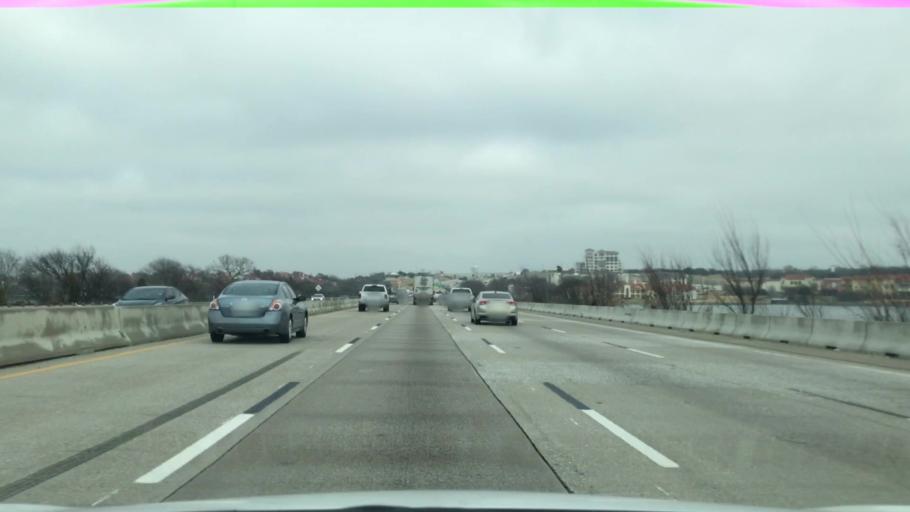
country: US
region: Texas
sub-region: Rockwall County
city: Rockwall
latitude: 32.8905
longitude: -96.4882
